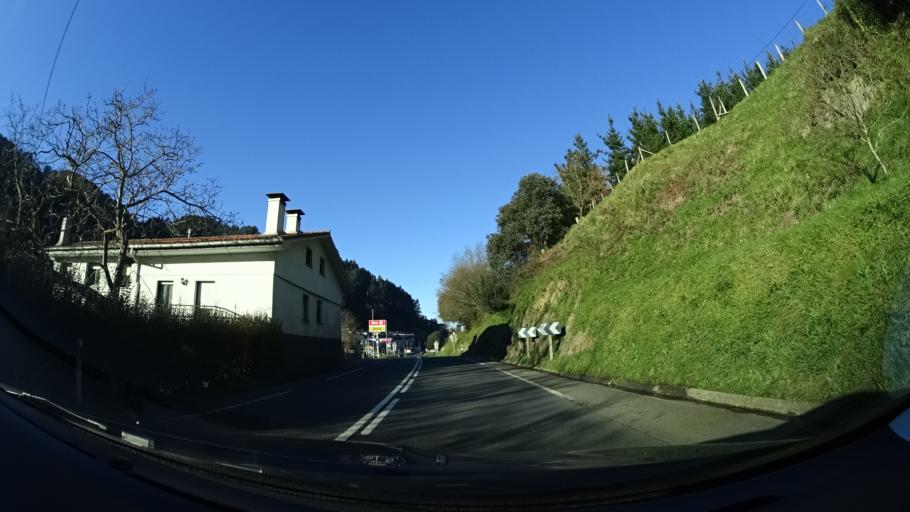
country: ES
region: Basque Country
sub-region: Bizkaia
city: Ondarroa
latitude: 43.3125
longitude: -2.4104
